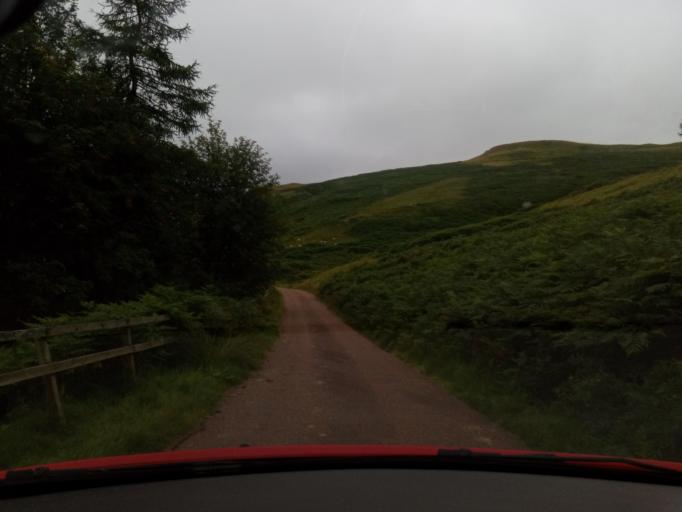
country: GB
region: England
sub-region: Northumberland
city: Rochester
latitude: 55.3698
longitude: -2.2144
